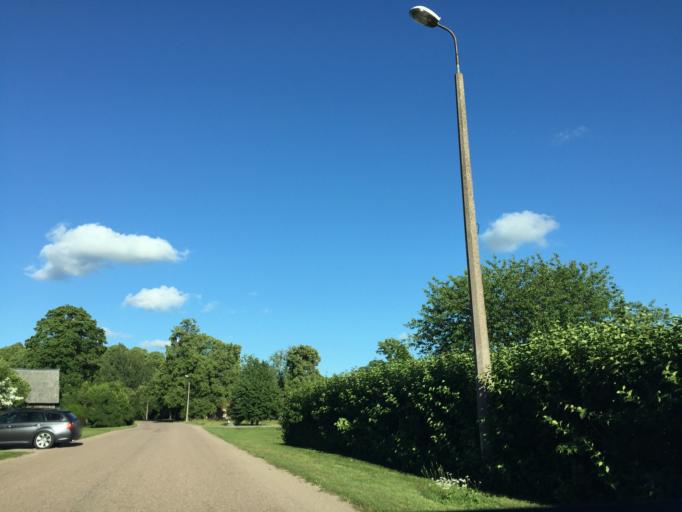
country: LV
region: Ventspils Rajons
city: Piltene
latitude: 57.3977
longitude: 21.8494
